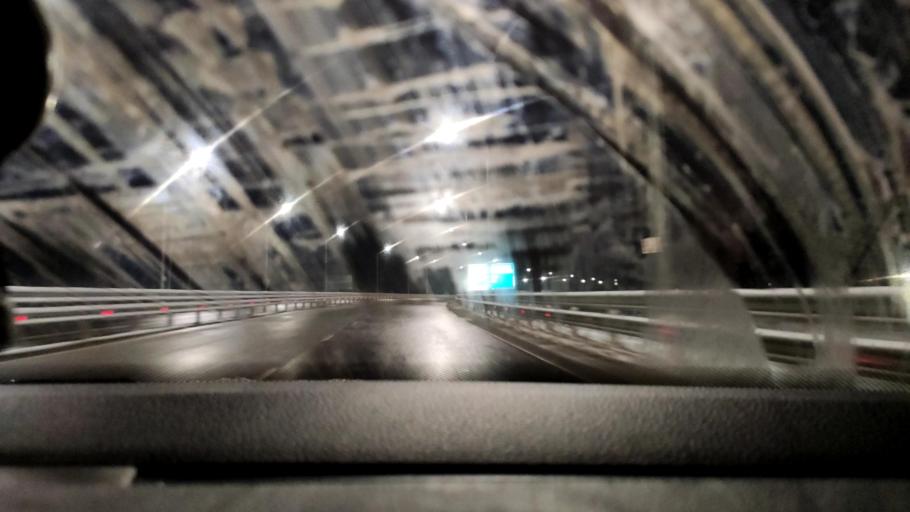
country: RU
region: Moskovskaya
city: Solnechnogorsk
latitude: 56.1633
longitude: 36.9167
